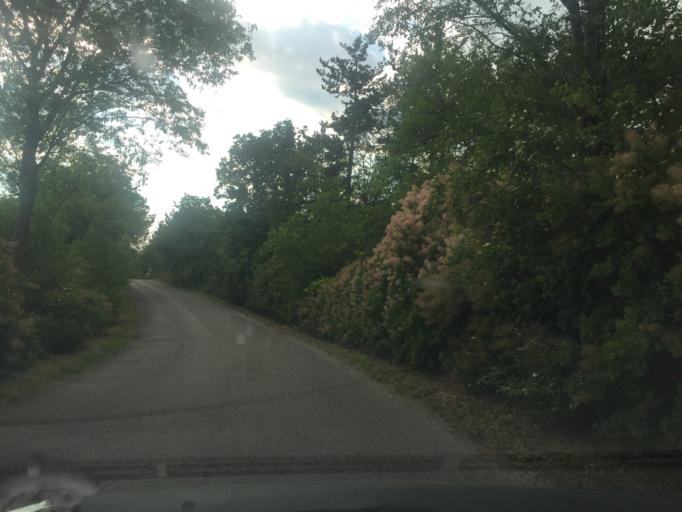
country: IT
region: Friuli Venezia Giulia
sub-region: Provincia di Gorizia
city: Doberdo del Lago
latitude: 45.8753
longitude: 13.5422
